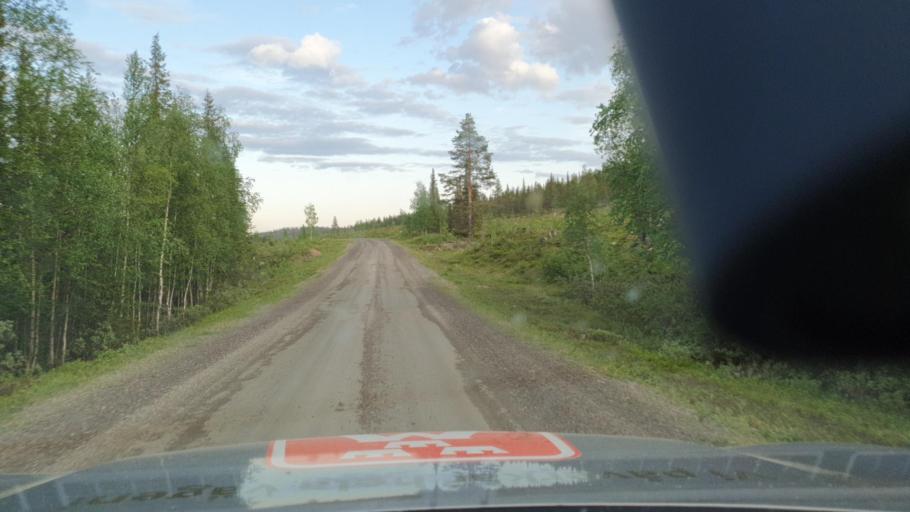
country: SE
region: Norrbotten
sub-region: Bodens Kommun
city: Boden
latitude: 66.5348
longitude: 21.4747
